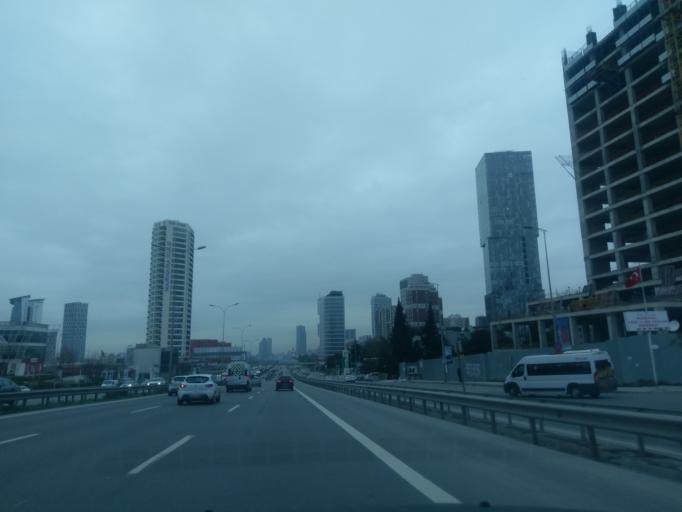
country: TR
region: Istanbul
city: Maltepe
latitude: 40.9099
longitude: 29.2011
